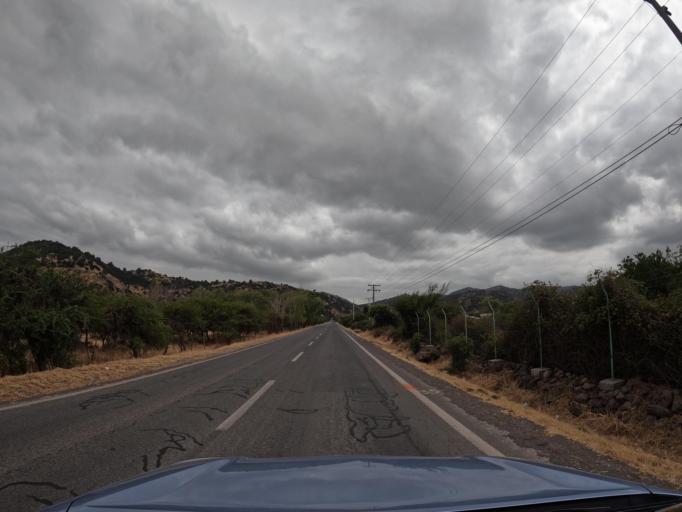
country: CL
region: Maule
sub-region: Provincia de Curico
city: Teno
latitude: -34.8313
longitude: -71.1901
